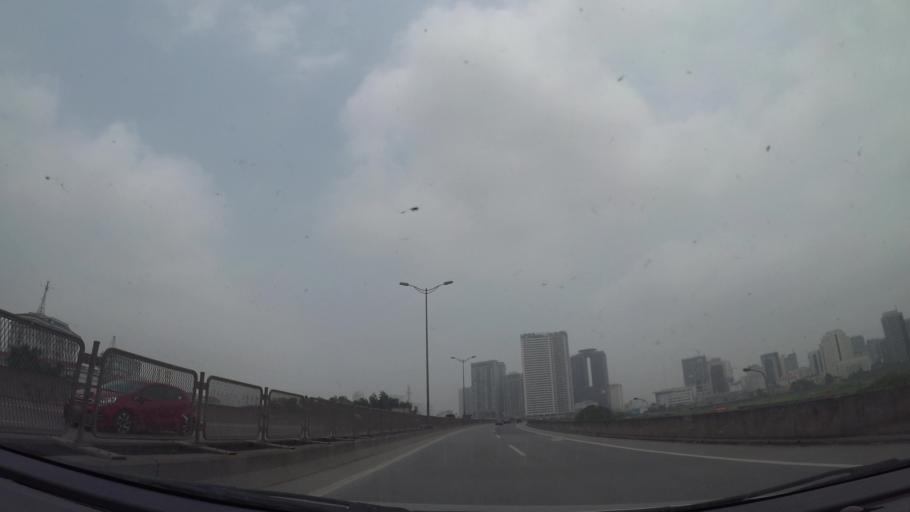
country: VN
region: Ha Noi
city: Cau Dien
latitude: 21.0222
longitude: 105.7792
